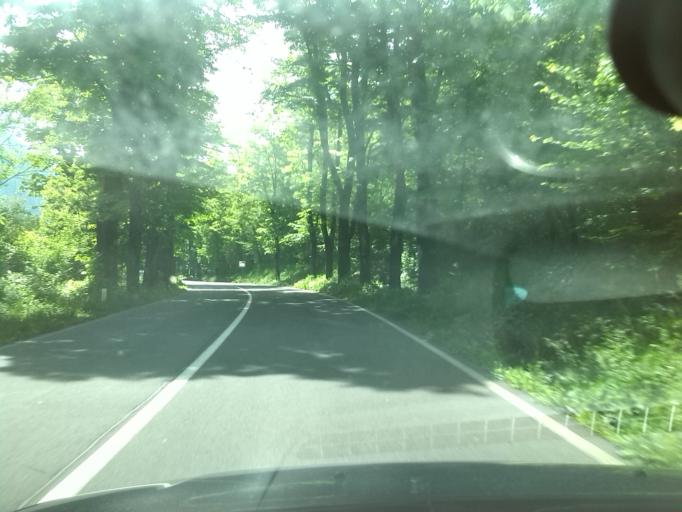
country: SI
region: Kobarid
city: Kobarid
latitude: 46.2499
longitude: 13.5663
